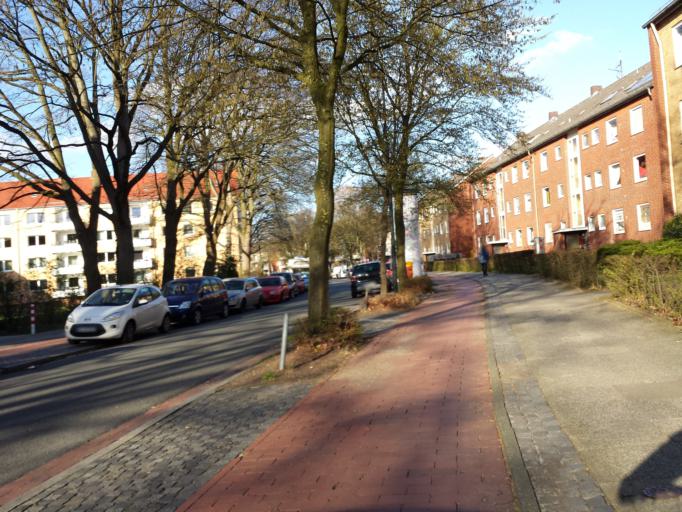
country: DE
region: Bremen
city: Bremen
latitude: 53.0890
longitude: 8.8525
